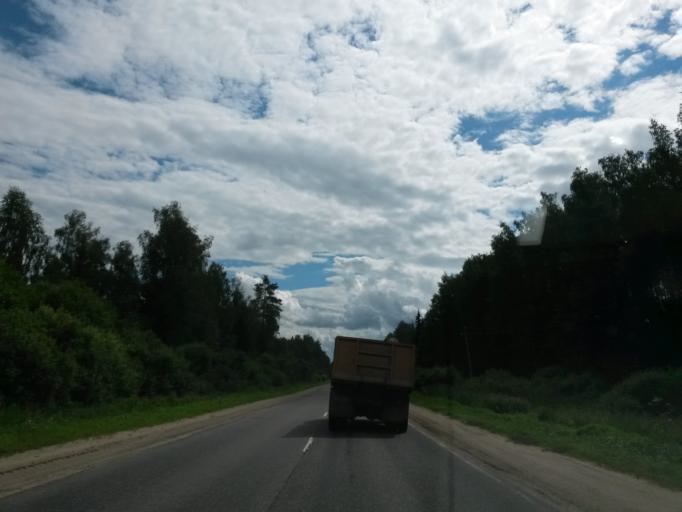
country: RU
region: Ivanovo
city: Novo-Talitsy
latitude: 57.0500
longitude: 40.7364
